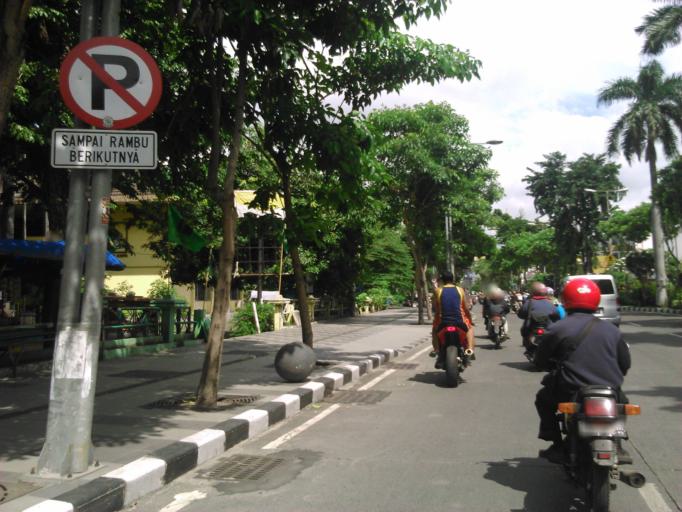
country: ID
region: East Java
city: Jagirsidosermo
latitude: -7.2927
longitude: 112.7292
